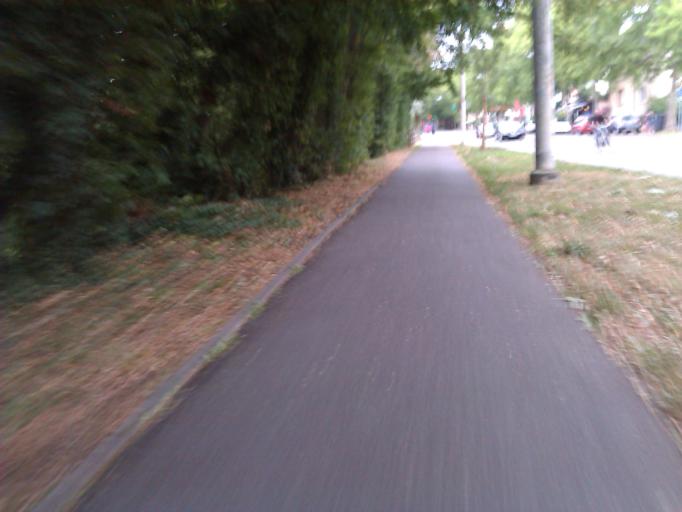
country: DE
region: Baden-Wuerttemberg
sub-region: Regierungsbezirk Stuttgart
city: Flein
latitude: 49.1220
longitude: 9.1939
